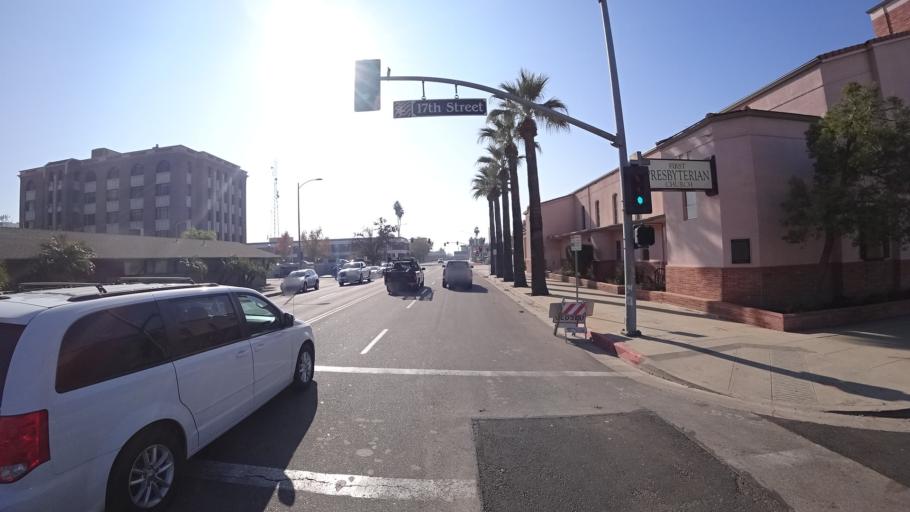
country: US
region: California
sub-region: Kern County
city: Bakersfield
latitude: 35.3743
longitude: -119.0213
